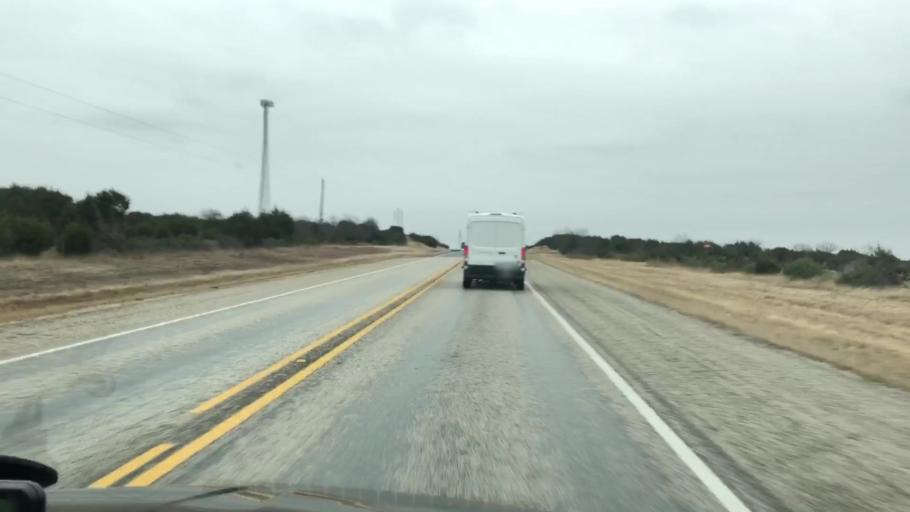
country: US
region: Texas
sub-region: Lampasas County
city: Lampasas
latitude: 31.1309
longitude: -98.1881
